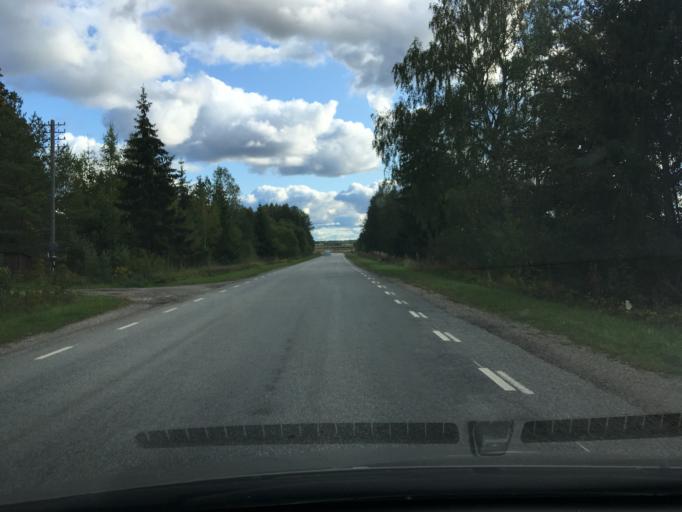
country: EE
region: Harju
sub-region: Raasiku vald
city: Raasiku
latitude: 59.3172
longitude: 25.1591
